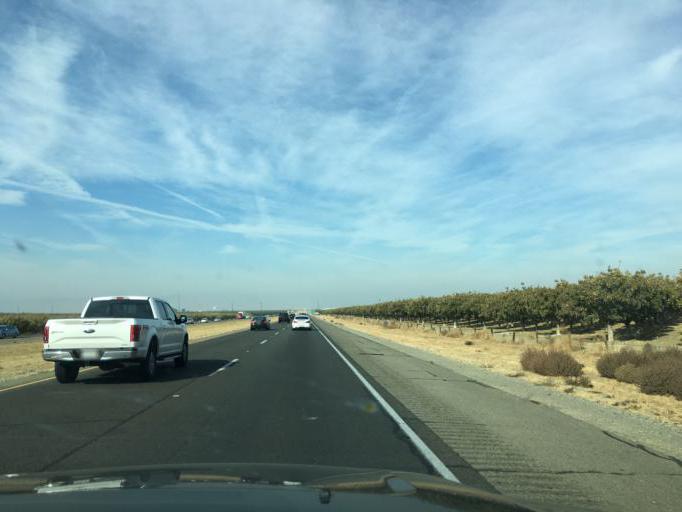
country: US
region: California
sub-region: Fresno County
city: Huron
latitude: 36.1183
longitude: -120.1408
